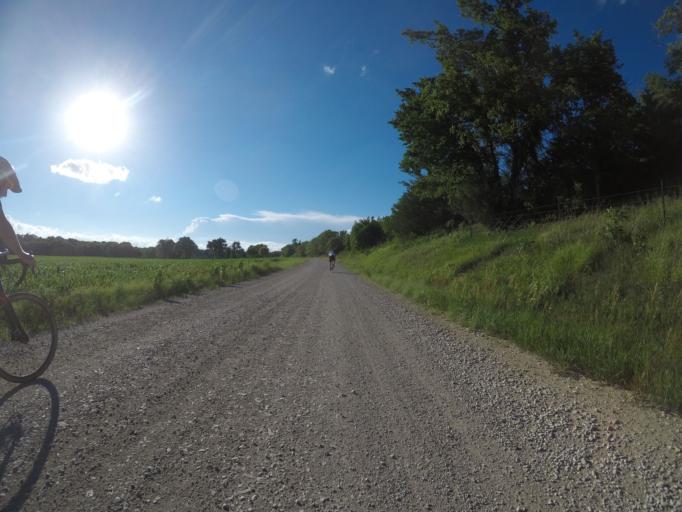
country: US
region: Kansas
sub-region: Riley County
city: Ogden
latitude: 39.2429
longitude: -96.7320
